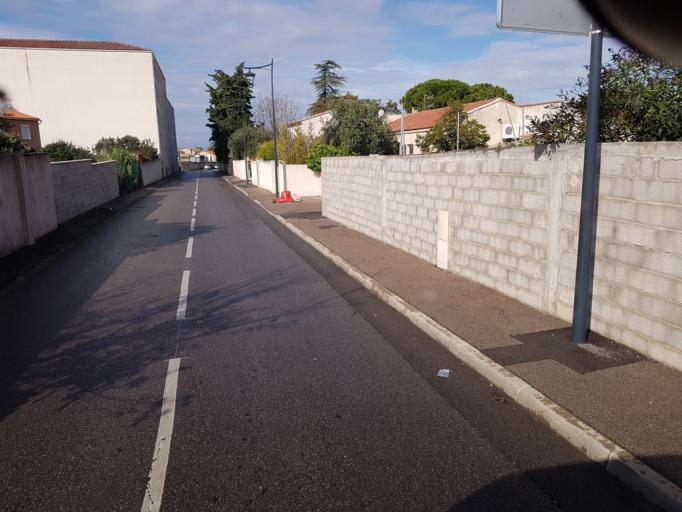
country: FR
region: Provence-Alpes-Cote d'Azur
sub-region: Departement des Bouches-du-Rhone
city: Gignac-la-Nerthe
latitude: 43.3908
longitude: 5.2359
